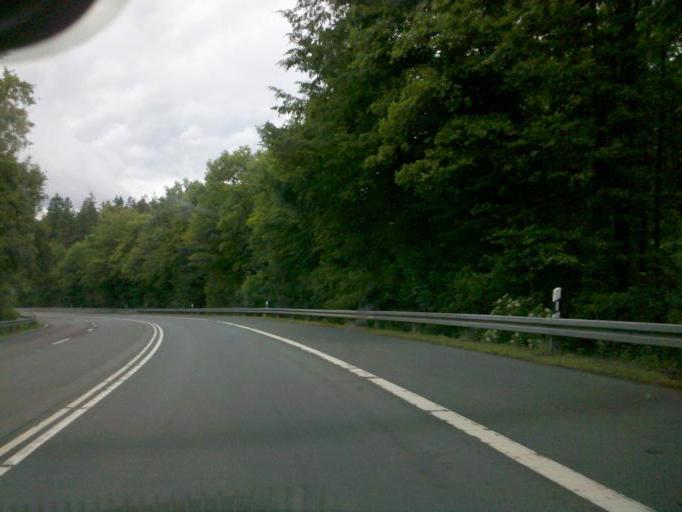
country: DE
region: North Rhine-Westphalia
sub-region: Regierungsbezirk Arnsberg
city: Meschede
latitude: 51.3755
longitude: 8.2931
